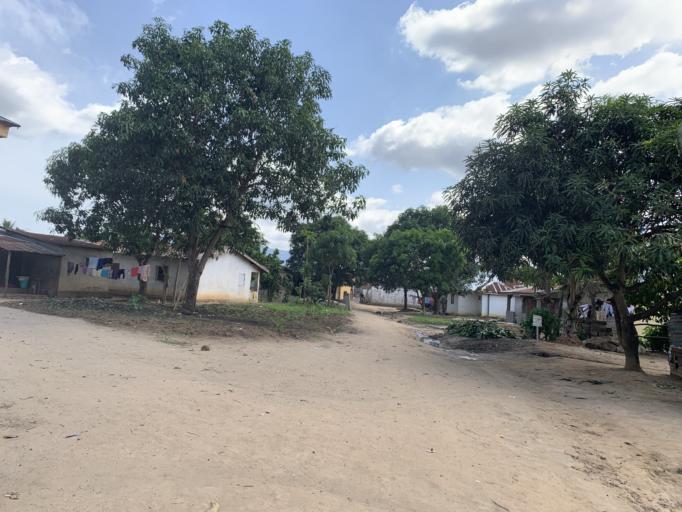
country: SL
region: Western Area
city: Waterloo
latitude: 8.3351
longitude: -13.0508
